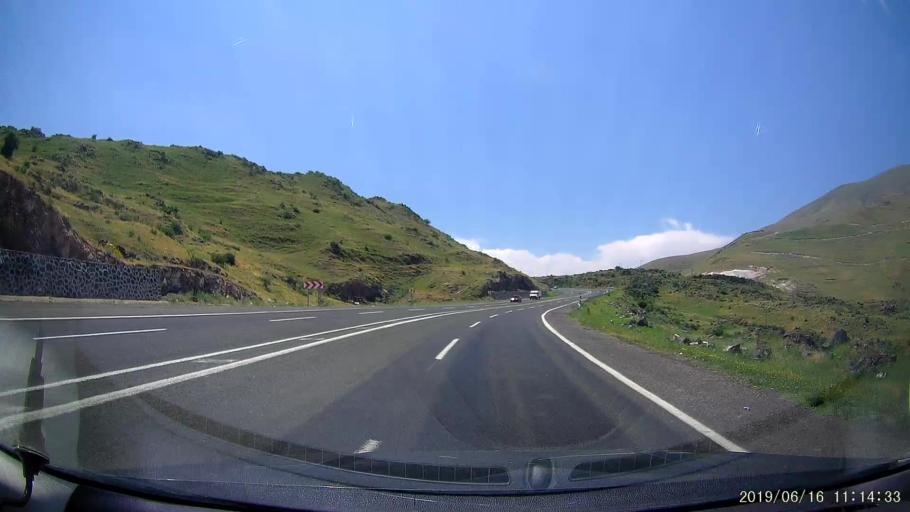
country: TR
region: Igdir
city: Igdir
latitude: 39.7770
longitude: 44.1423
